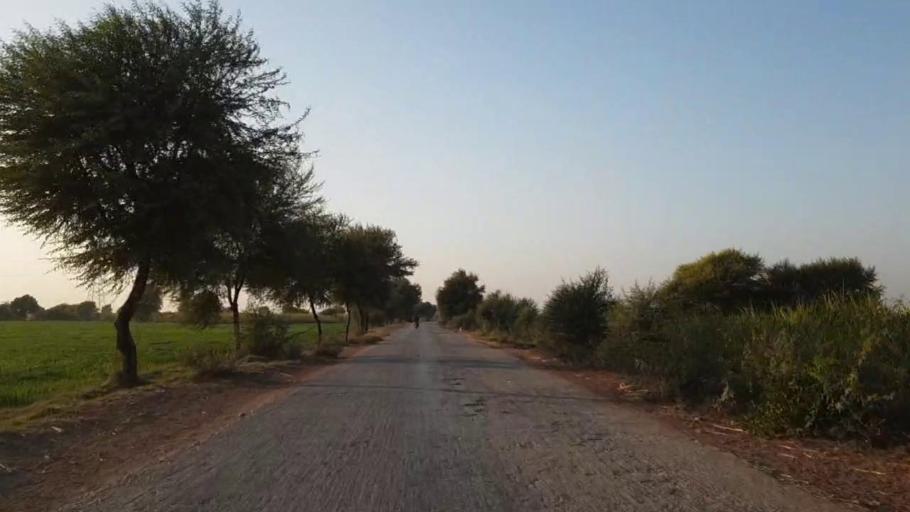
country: PK
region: Sindh
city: Chambar
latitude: 25.2285
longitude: 68.7096
